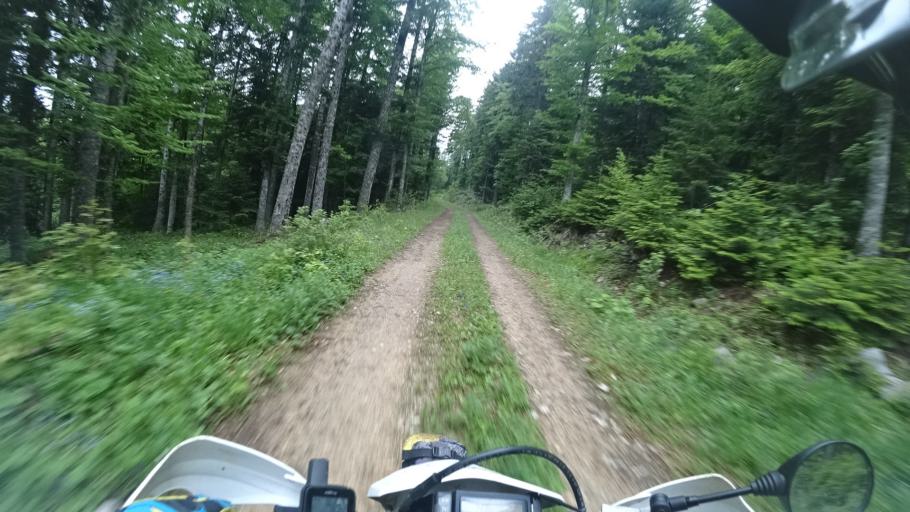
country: BA
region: Federation of Bosnia and Herzegovina
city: Bihac
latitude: 44.6269
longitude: 15.8135
